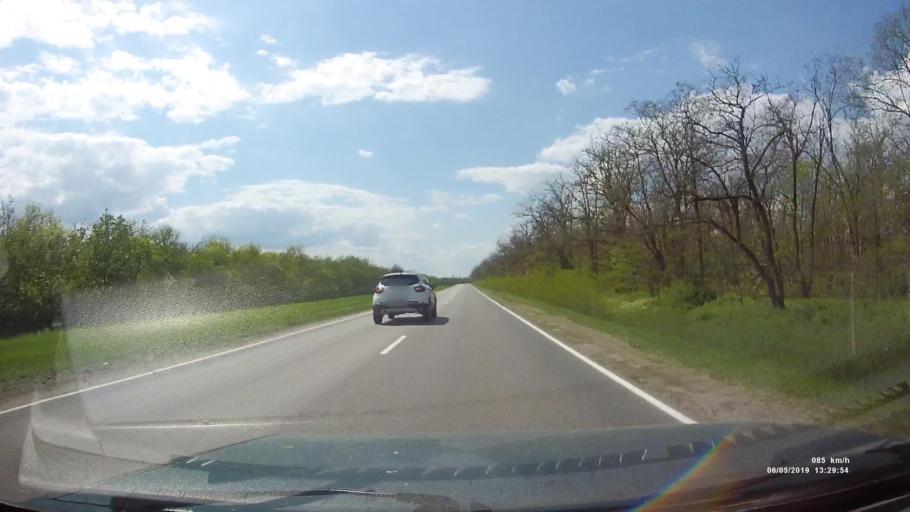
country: RU
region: Rostov
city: Ust'-Donetskiy
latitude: 47.6715
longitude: 40.8363
